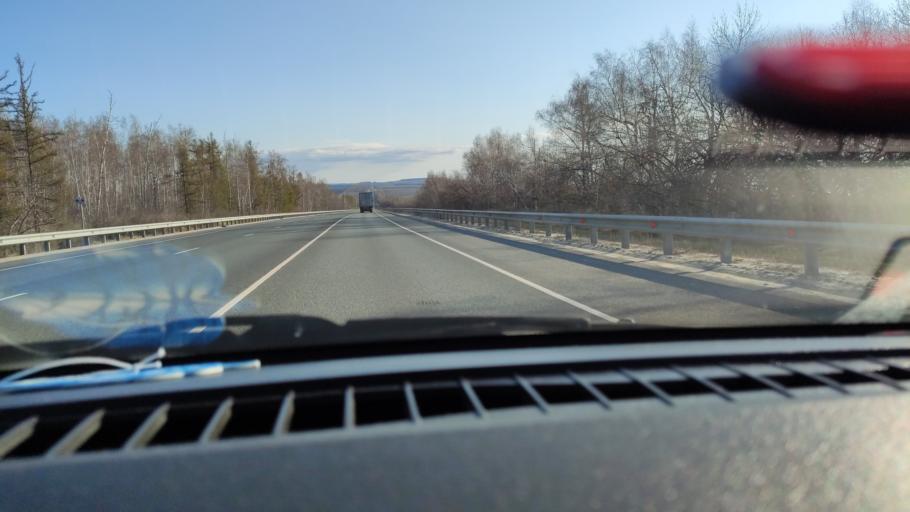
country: RU
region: Saratov
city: Khvalynsk
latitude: 52.5631
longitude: 48.0914
